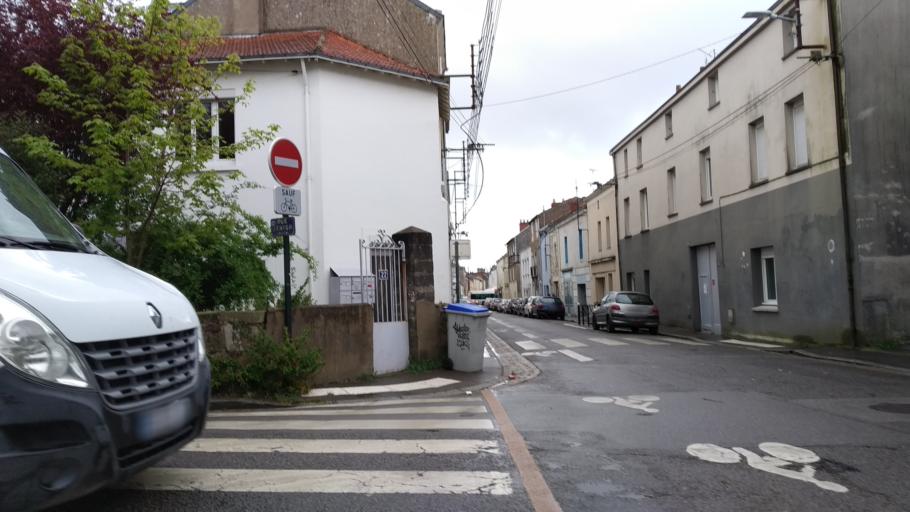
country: FR
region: Pays de la Loire
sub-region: Departement de la Loire-Atlantique
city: Nantes
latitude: 47.2109
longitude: -1.5886
